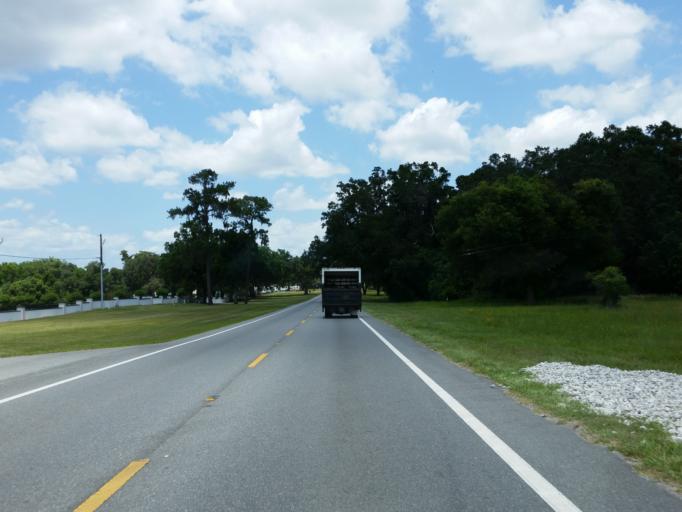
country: US
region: Florida
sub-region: Marion County
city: Belleview
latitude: 28.9974
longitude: -82.0413
